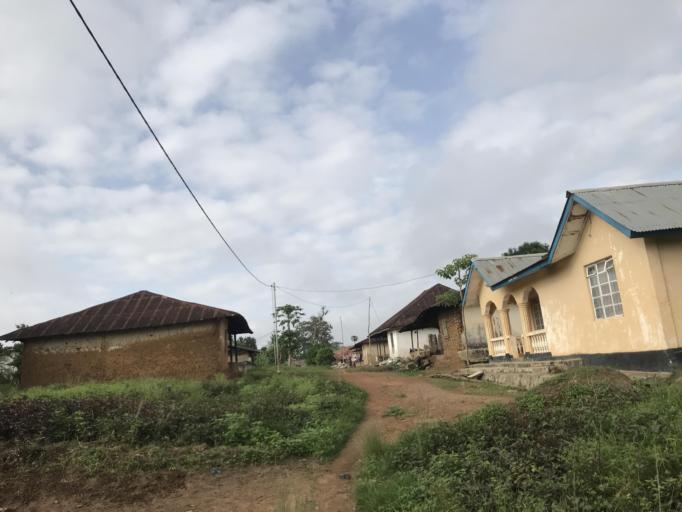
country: SL
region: Eastern Province
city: Pendembu
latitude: 8.1007
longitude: -10.6954
